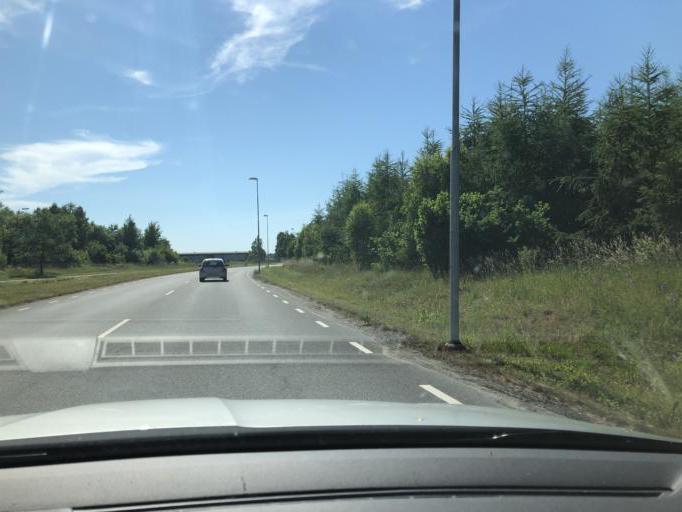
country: SE
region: Skane
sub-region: Bromolla Kommun
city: Bromoella
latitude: 56.0762
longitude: 14.4964
